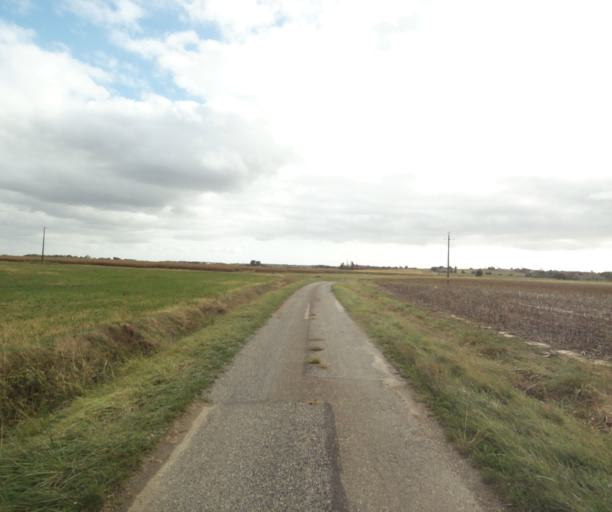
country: FR
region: Midi-Pyrenees
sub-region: Departement du Tarn-et-Garonne
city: Beaumont-de-Lomagne
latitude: 43.8885
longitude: 1.0871
